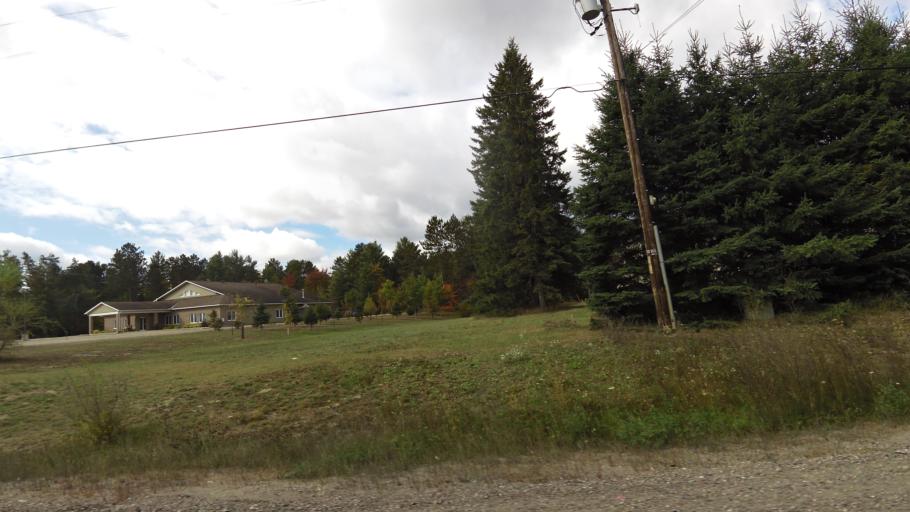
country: CA
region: Ontario
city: Deep River
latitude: 46.0926
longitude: -77.4909
